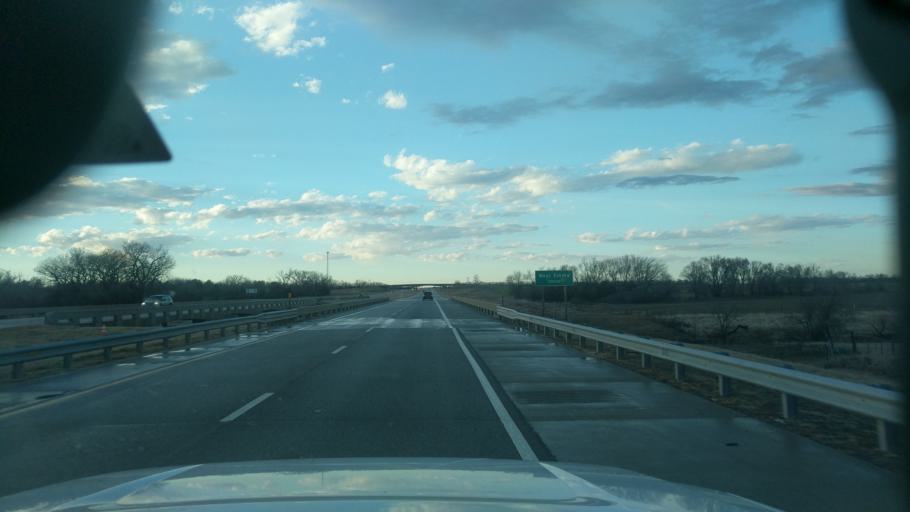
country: US
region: Kansas
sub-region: Harvey County
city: Hesston
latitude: 38.1841
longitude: -97.4620
